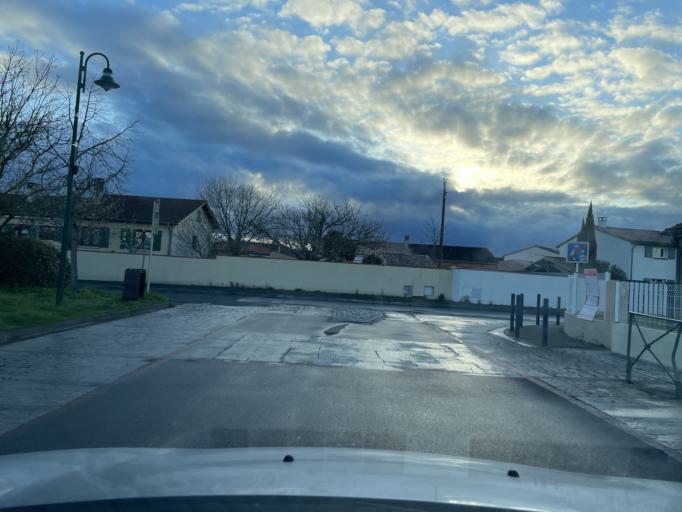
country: FR
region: Midi-Pyrenees
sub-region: Departement de la Haute-Garonne
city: Pibrac
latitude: 43.6122
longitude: 1.2868
